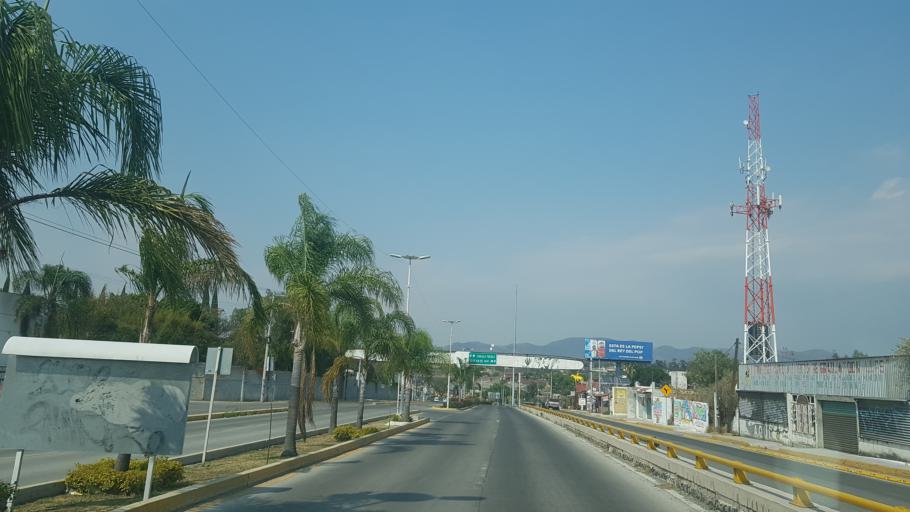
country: MX
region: Puebla
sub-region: Atlixco
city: El Encanto del Cerril
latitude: 18.9239
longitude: -98.4131
